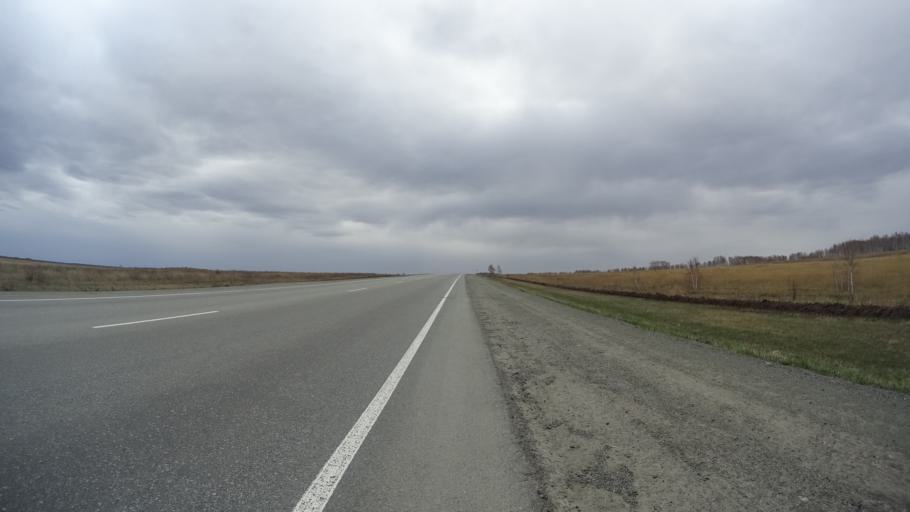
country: RU
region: Chelyabinsk
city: Yemanzhelinsk
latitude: 54.7084
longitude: 61.2583
